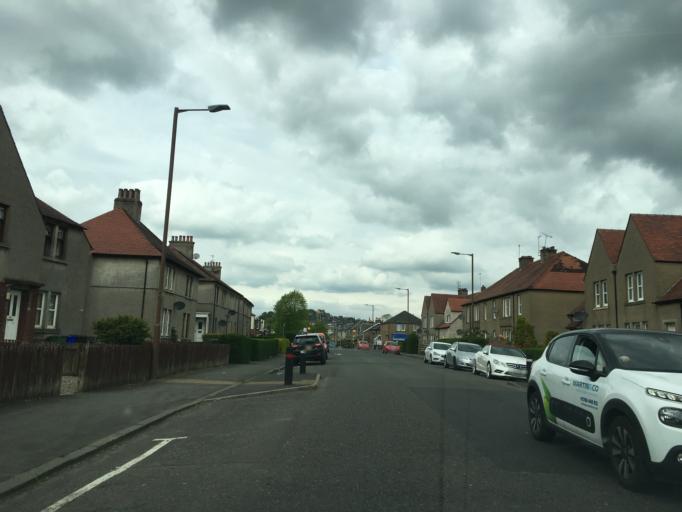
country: GB
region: Scotland
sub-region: Stirling
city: Stirling
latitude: 56.1105
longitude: -3.9296
